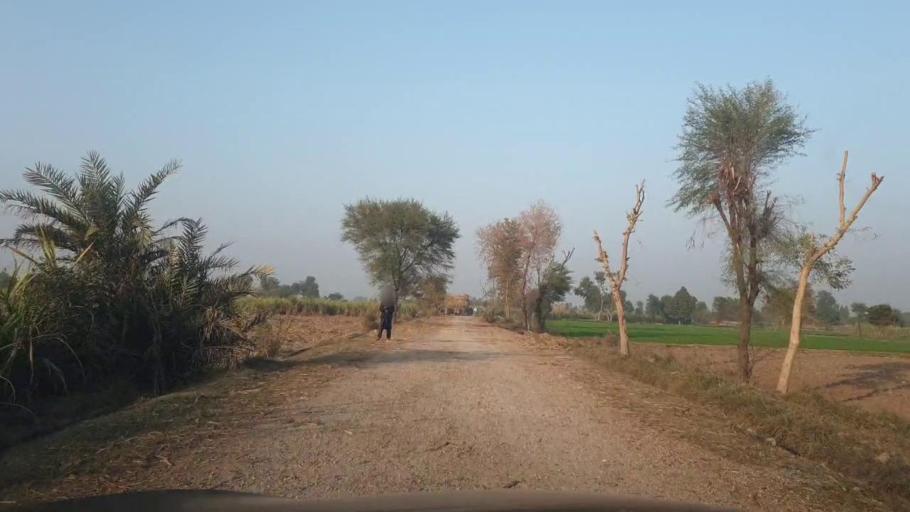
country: PK
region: Sindh
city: Ubauro
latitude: 28.3248
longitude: 69.7762
